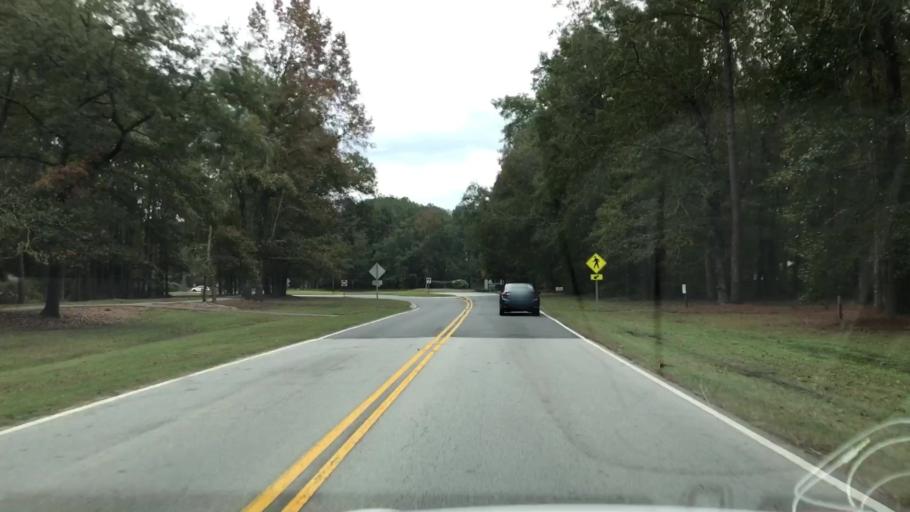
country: US
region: South Carolina
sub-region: Berkeley County
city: Goose Creek
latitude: 33.0081
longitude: -80.0564
